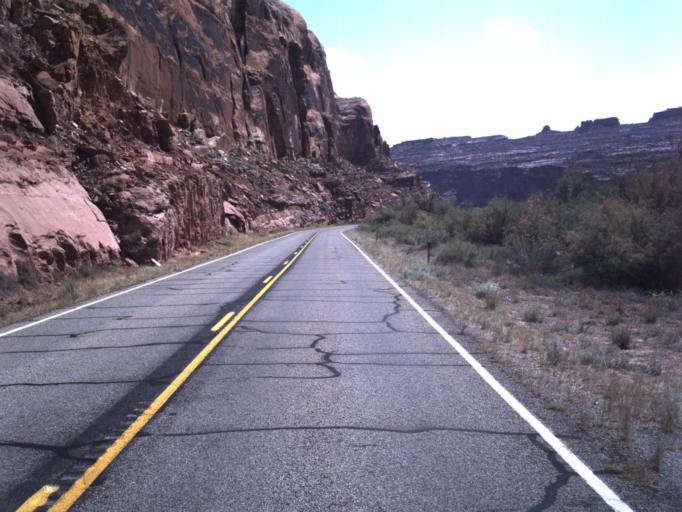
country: US
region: Utah
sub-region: Grand County
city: Moab
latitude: 38.5555
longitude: -109.6313
